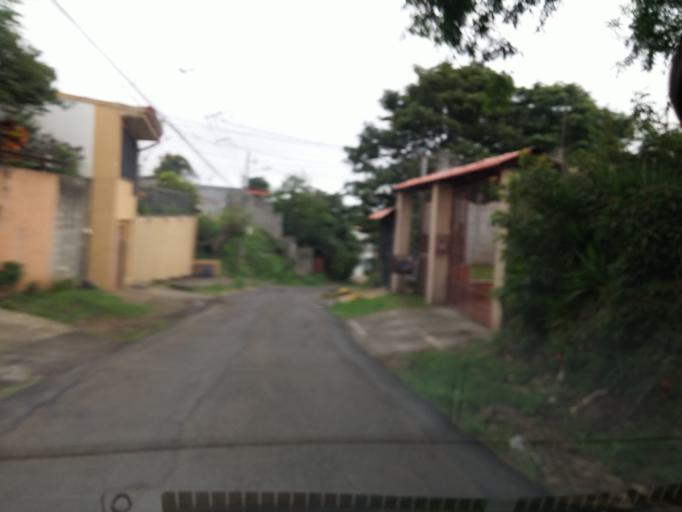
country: CR
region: Heredia
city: San Josecito
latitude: 10.0295
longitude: -84.0972
